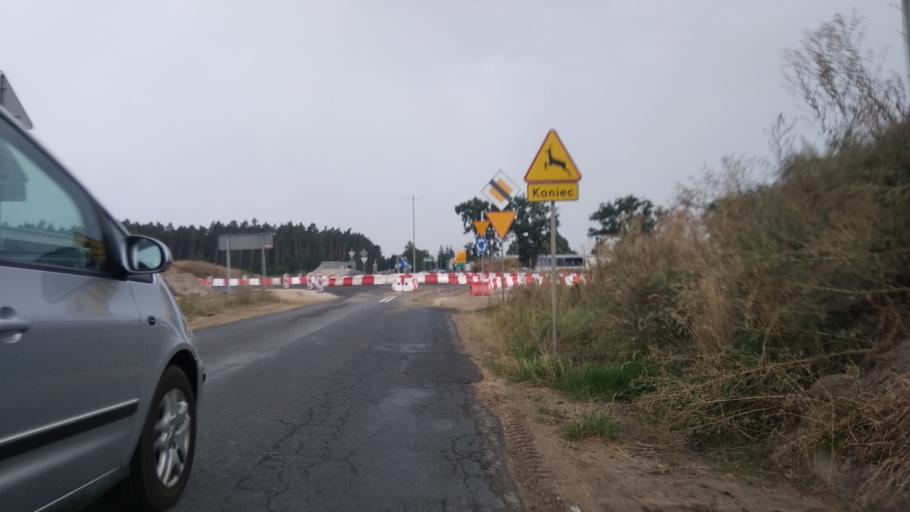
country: PL
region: Kujawsko-Pomorskie
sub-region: Powiat bydgoski
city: Osielsko
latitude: 53.2225
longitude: 18.1293
